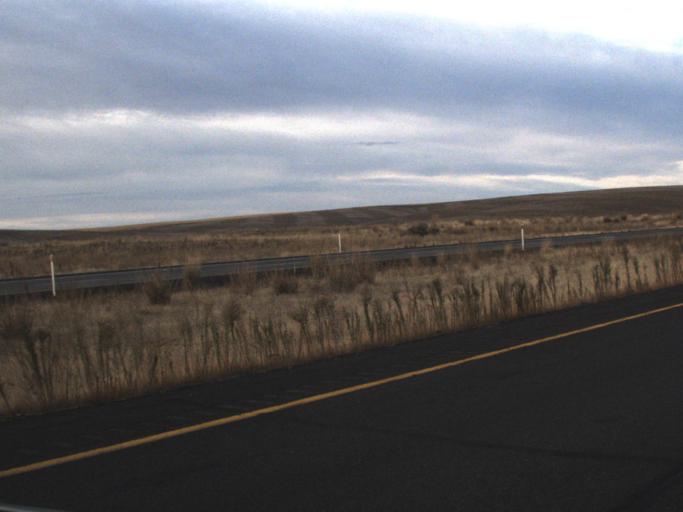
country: US
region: Washington
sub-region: Franklin County
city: Connell
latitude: 46.8223
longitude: -118.6761
